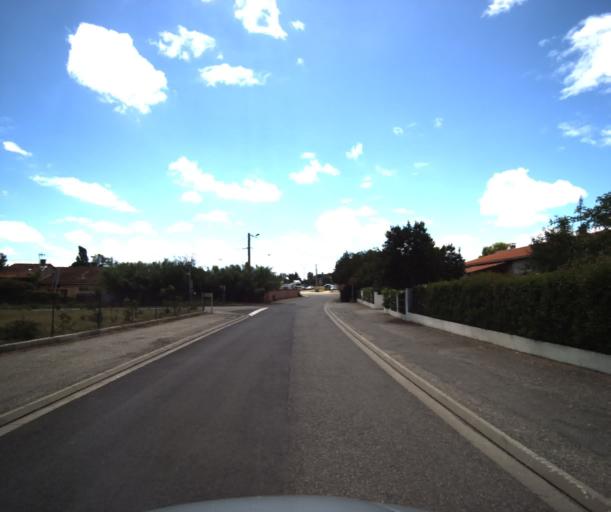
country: FR
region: Midi-Pyrenees
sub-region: Departement de la Haute-Garonne
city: Lacroix-Falgarde
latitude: 43.4855
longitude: 1.4021
